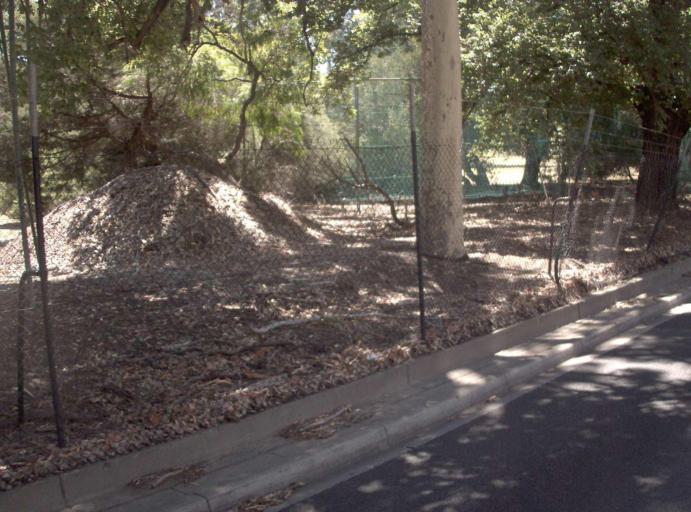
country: AU
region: Victoria
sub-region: Port Phillip
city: South Melbourne
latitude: -37.8424
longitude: 144.9753
